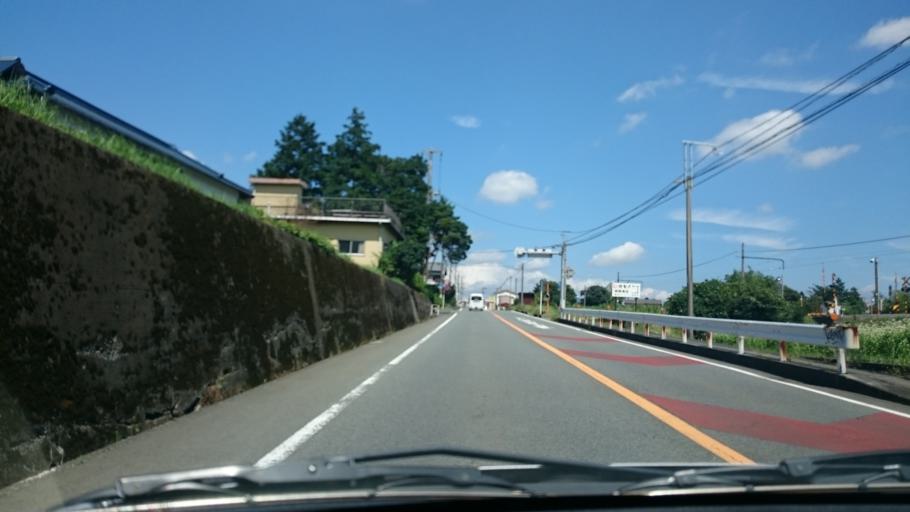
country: JP
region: Shizuoka
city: Gotemba
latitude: 35.2734
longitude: 138.9239
